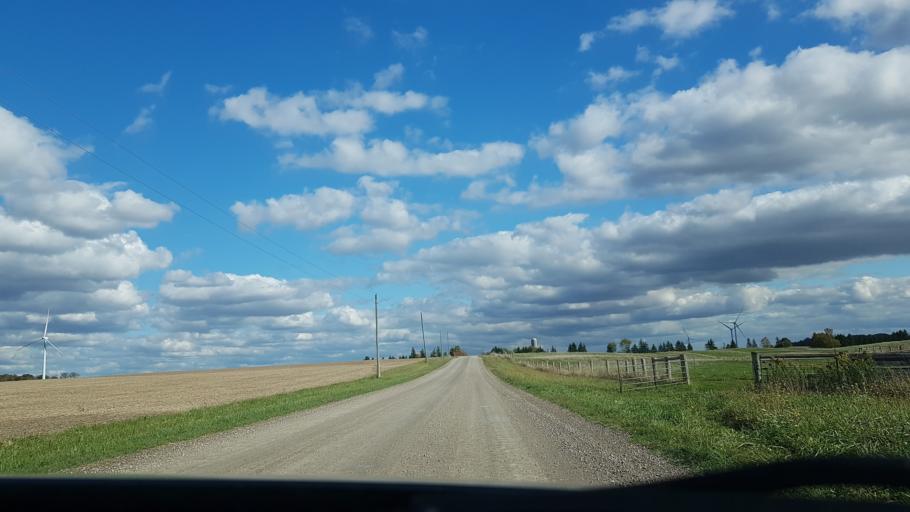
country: CA
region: Ontario
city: South Huron
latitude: 43.1156
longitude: -81.6658
